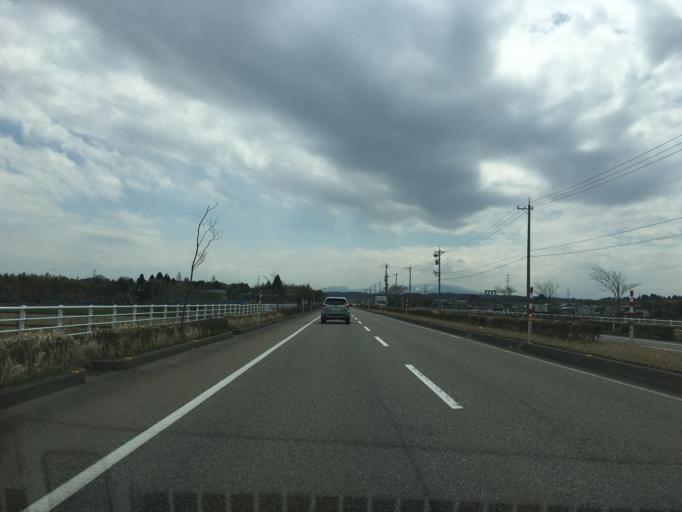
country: JP
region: Toyama
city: Kuragaki-kosugi
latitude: 36.7073
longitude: 137.1159
